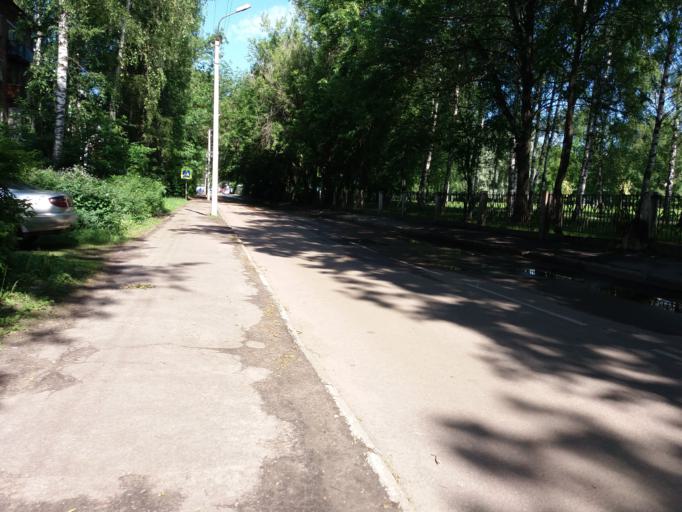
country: RU
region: Jaroslavl
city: Yaroslavl
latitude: 57.6362
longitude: 39.8525
